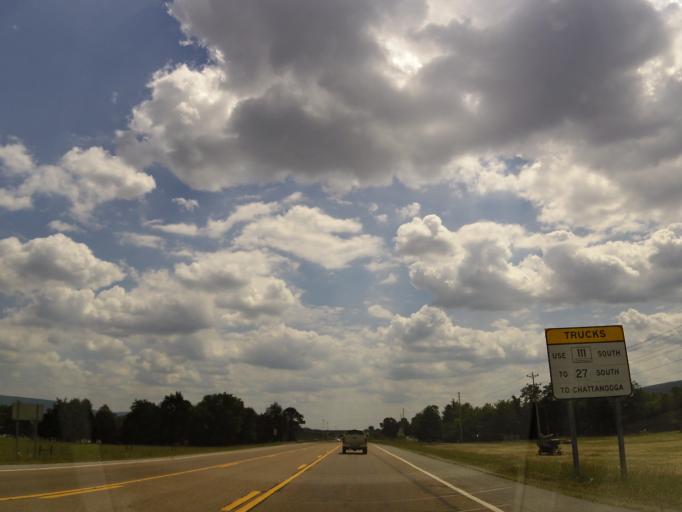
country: US
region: Tennessee
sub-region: Sequatchie County
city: Dunlap
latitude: 35.4000
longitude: -85.3718
